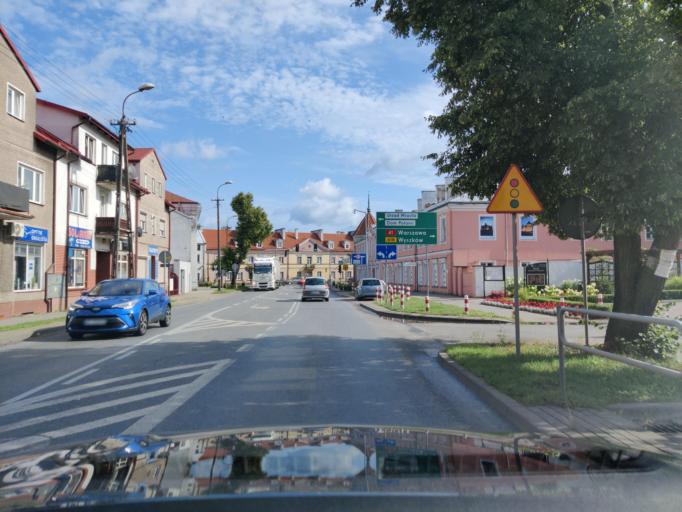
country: PL
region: Masovian Voivodeship
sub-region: Powiat pultuski
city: Pultusk
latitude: 52.7048
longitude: 21.0864
